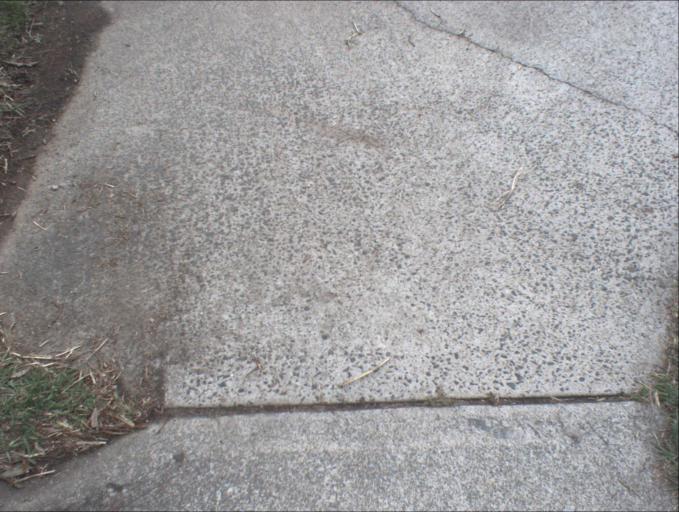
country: AU
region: Queensland
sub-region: Brisbane
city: Sunnybank Hills
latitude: -27.6669
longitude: 153.0517
